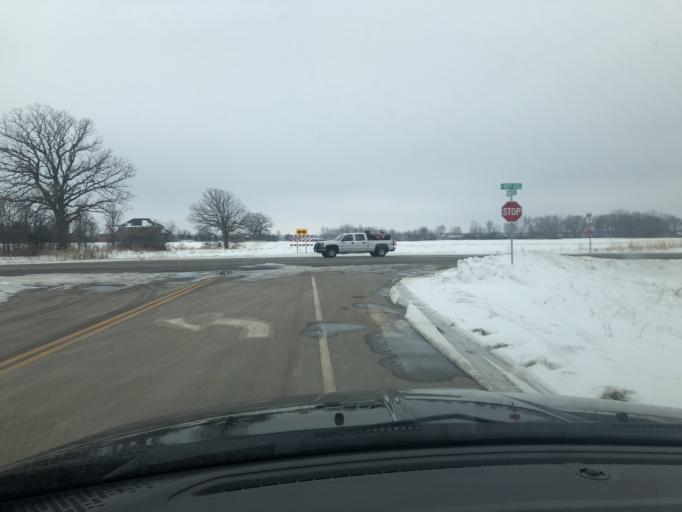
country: US
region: Minnesota
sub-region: Washington County
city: Lake Elmo
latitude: 45.0073
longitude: -92.8585
